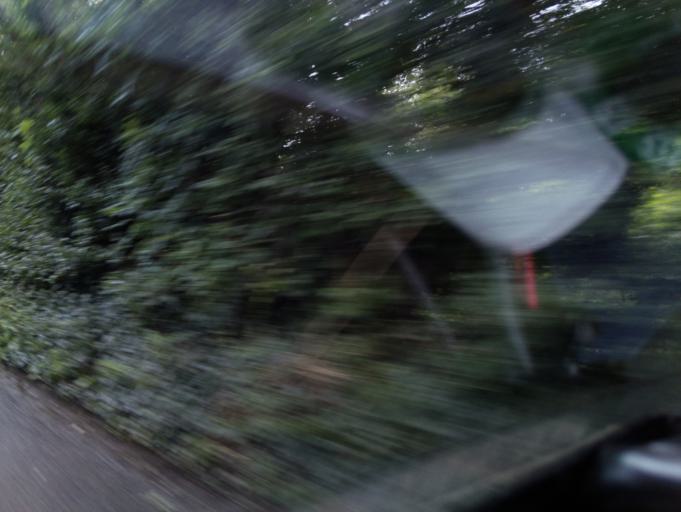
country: GB
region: England
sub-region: Devon
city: Modbury
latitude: 50.3470
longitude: -3.8886
